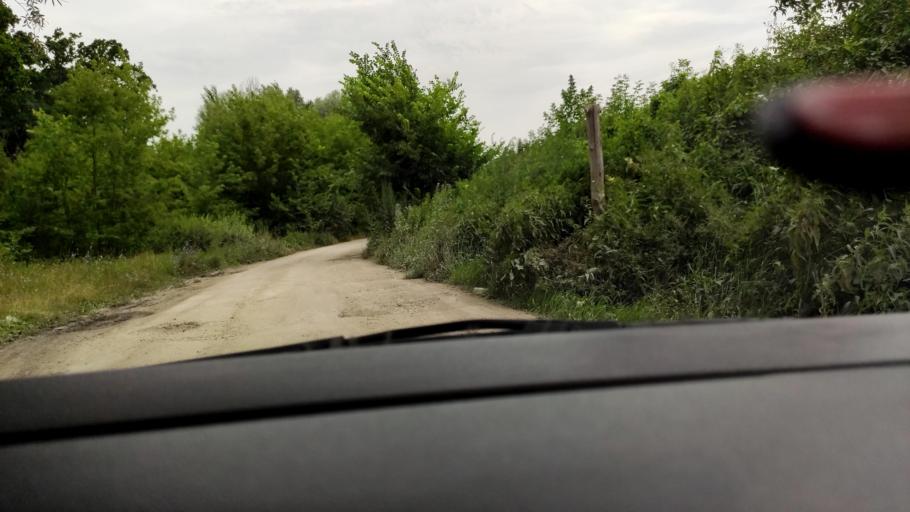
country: RU
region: Voronezj
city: Ramon'
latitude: 51.8916
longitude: 39.3524
